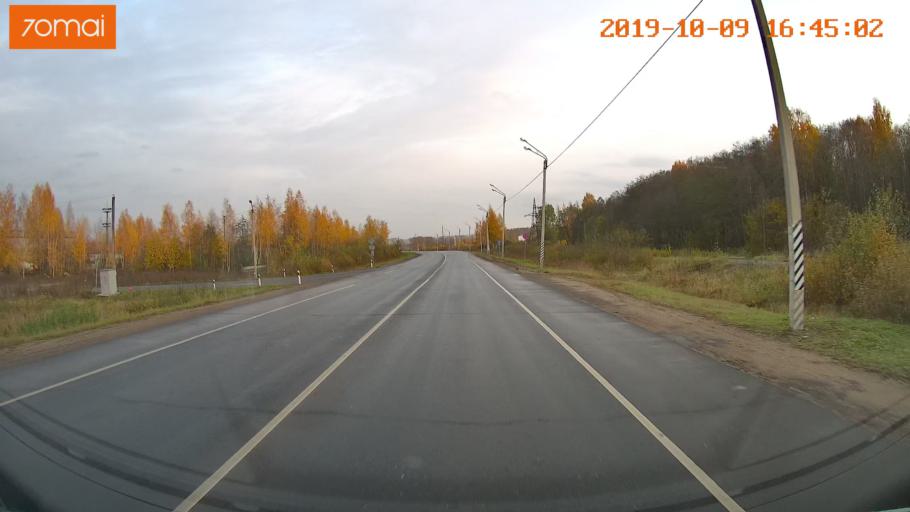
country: RU
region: Kostroma
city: Volgorechensk
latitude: 57.4487
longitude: 41.1488
